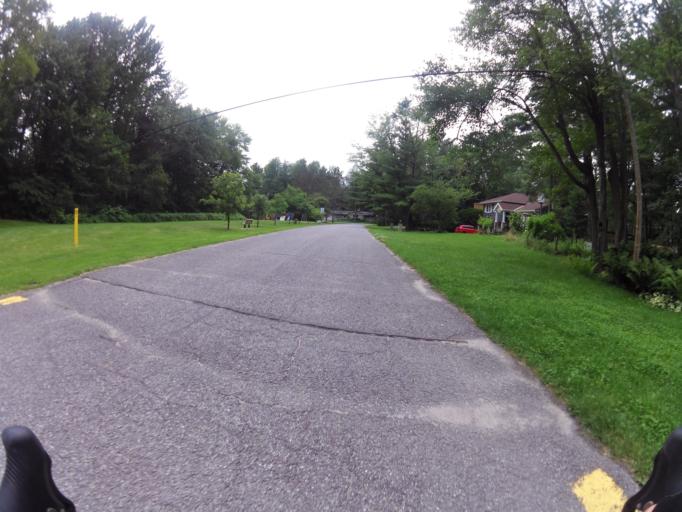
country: CA
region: Ontario
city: Ottawa
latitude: 45.3260
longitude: -75.7086
